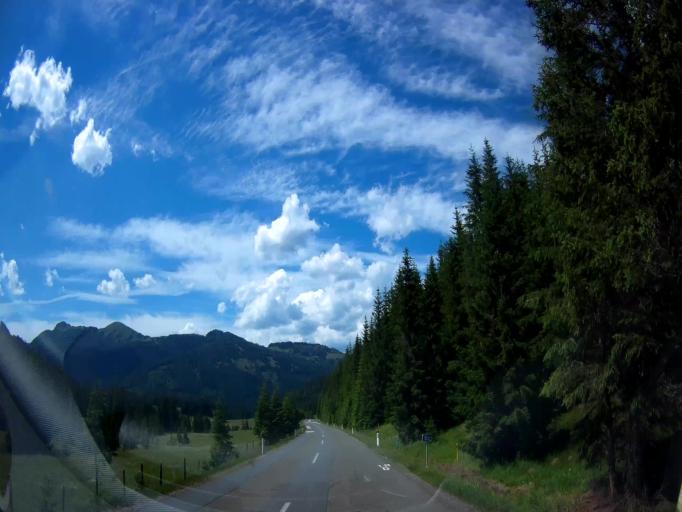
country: AT
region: Styria
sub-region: Politischer Bezirk Murau
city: Stadl an der Mur
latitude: 46.9641
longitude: 14.0218
